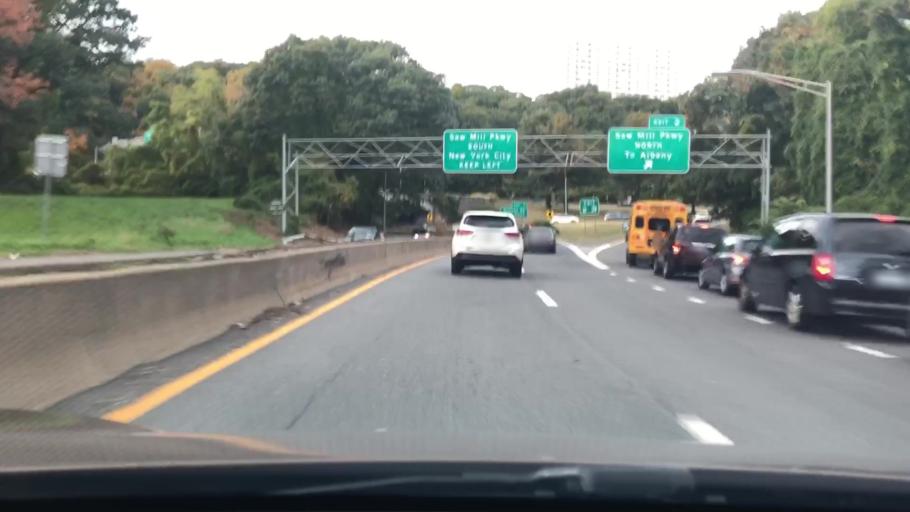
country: US
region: New York
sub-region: Westchester County
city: Yonkers
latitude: 40.9321
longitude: -73.8774
